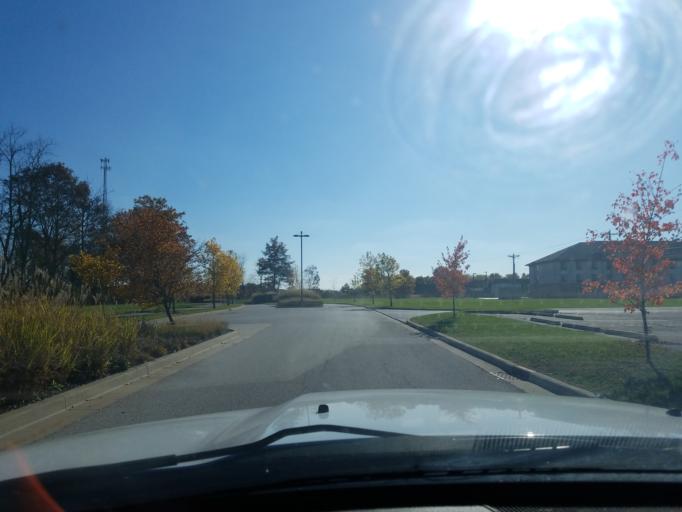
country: US
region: Indiana
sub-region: Montgomery County
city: Crawfordsville
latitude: 40.0755
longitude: -86.9039
